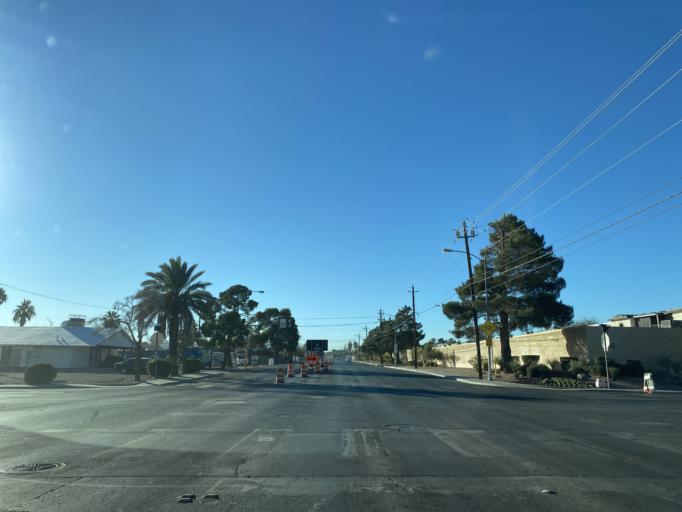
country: US
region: Nevada
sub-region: Clark County
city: Winchester
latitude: 36.1226
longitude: -115.0919
